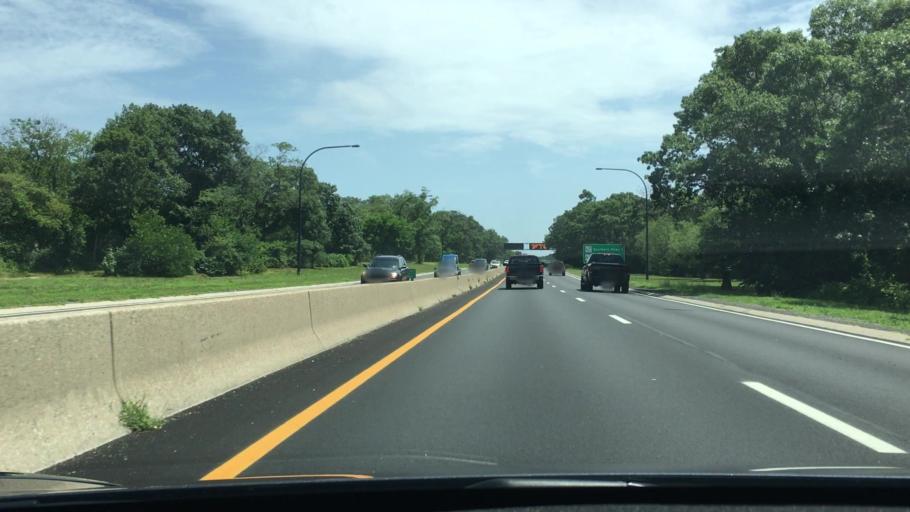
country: US
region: New York
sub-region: Nassau County
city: Levittown
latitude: 40.7143
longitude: -73.5303
